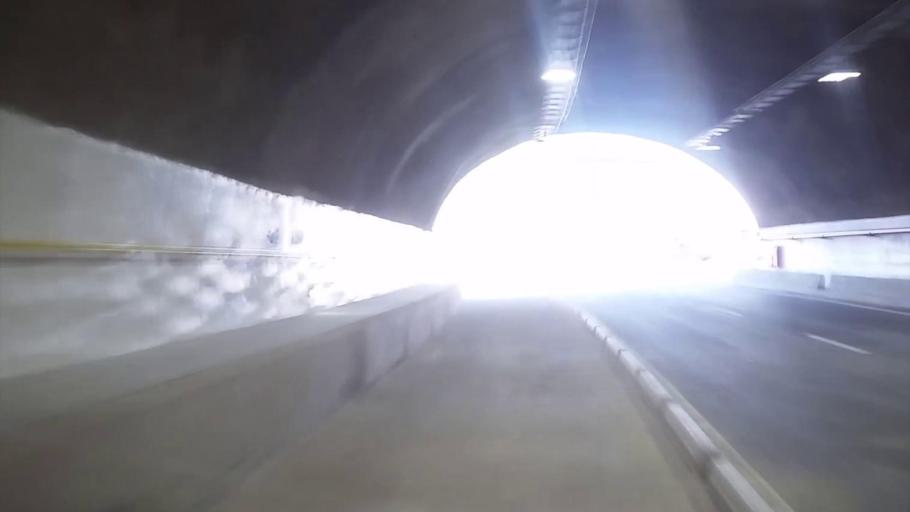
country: BR
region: Rio de Janeiro
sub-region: Nilopolis
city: Nilopolis
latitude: -22.9016
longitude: -43.3985
